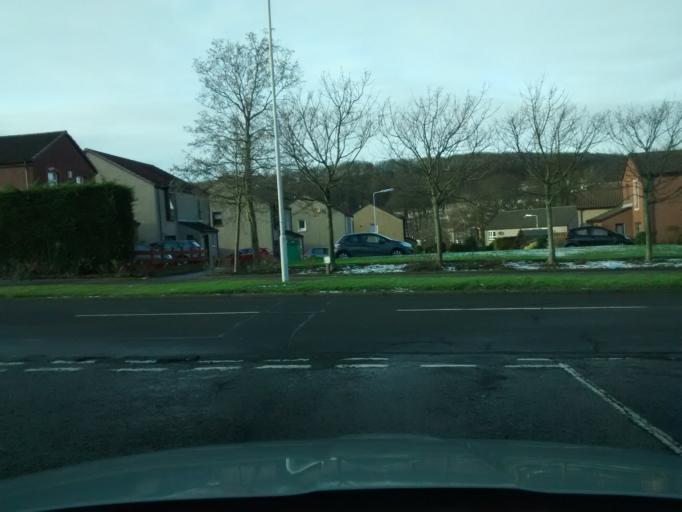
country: GB
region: Scotland
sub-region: Fife
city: Inverkeithing
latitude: 56.0335
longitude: -3.3630
